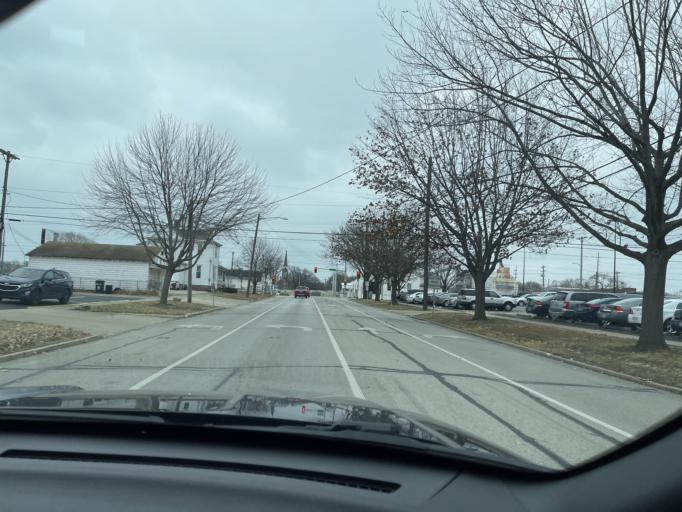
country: US
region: Illinois
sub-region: Sangamon County
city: Springfield
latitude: 39.7938
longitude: -89.6450
